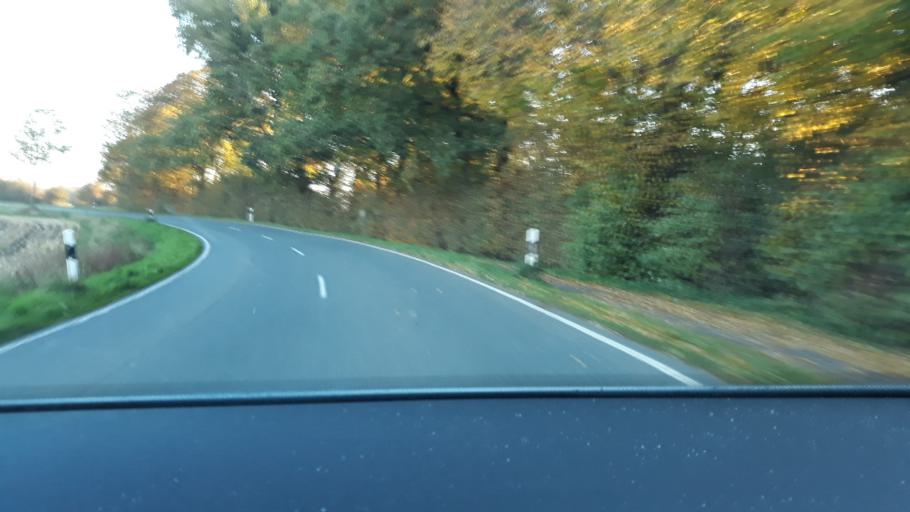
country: DE
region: Schleswig-Holstein
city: Satrup
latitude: 54.6718
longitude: 9.6059
